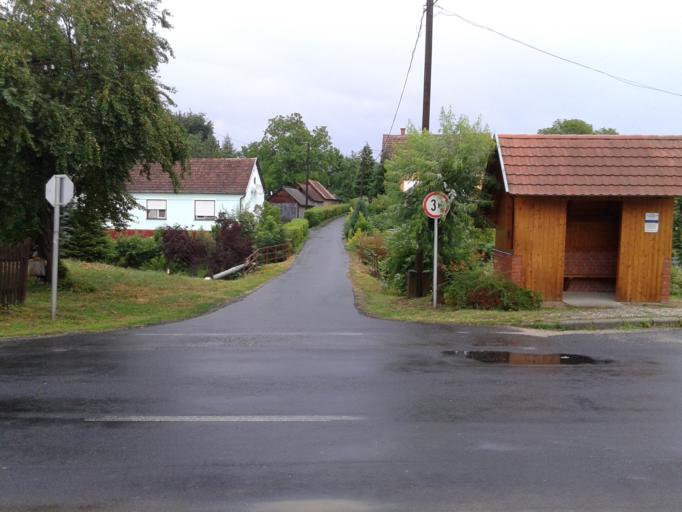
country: AT
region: Burgenland
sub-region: Politischer Bezirk Gussing
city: Heiligenbrunn
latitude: 46.9351
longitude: 16.4971
